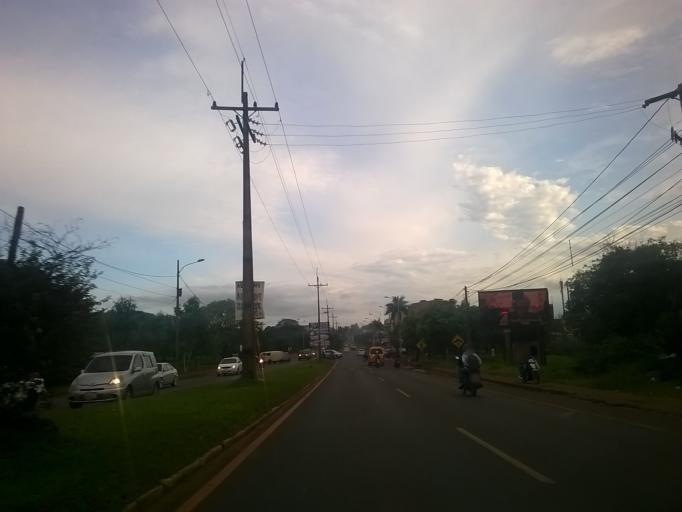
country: PY
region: Alto Parana
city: Presidente Franco
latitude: -25.5272
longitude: -54.6369
